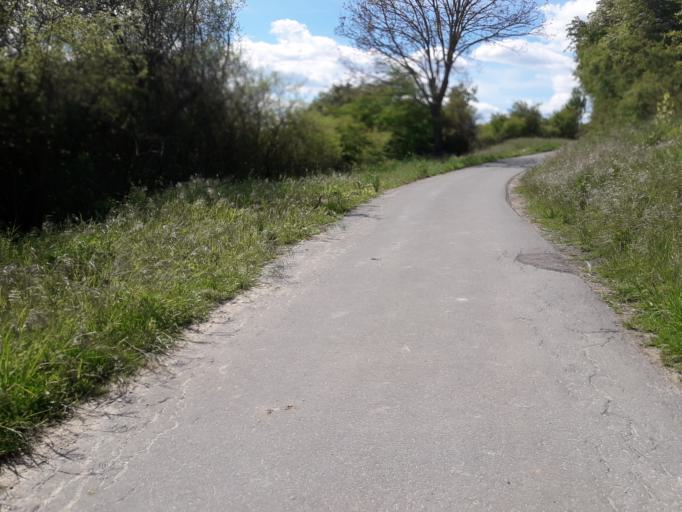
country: DE
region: North Rhine-Westphalia
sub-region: Regierungsbezirk Detmold
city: Paderborn
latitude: 51.6967
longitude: 8.8090
